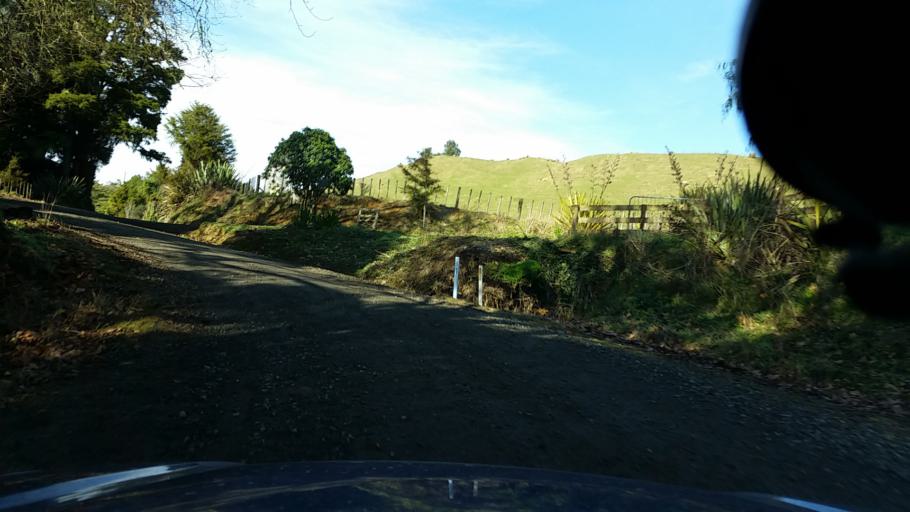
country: NZ
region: Taranaki
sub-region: New Plymouth District
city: Waitara
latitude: -39.0593
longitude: 174.7815
